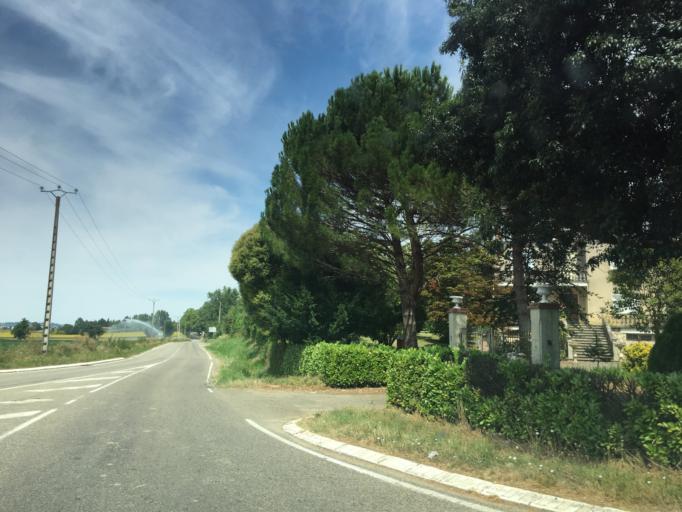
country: FR
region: Midi-Pyrenees
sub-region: Departement du Gers
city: Fleurance
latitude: 43.8489
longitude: 0.6769
